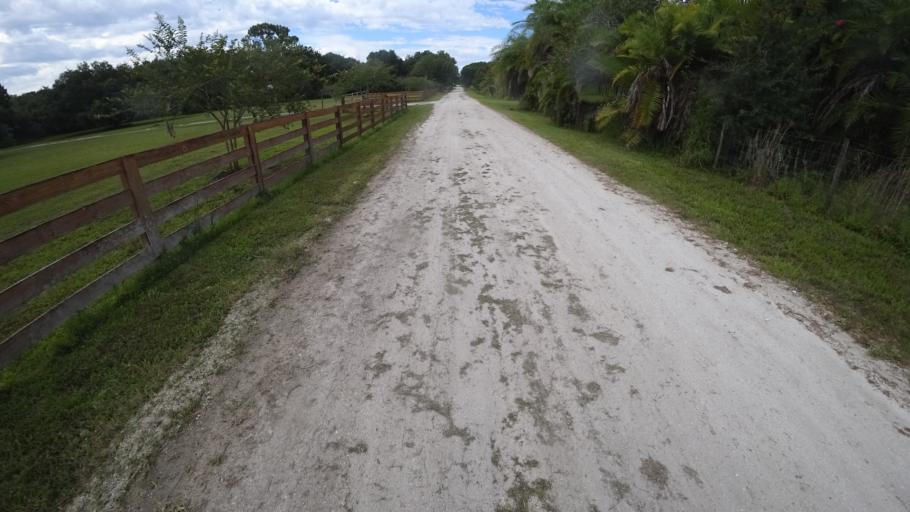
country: US
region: Florida
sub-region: Sarasota County
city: The Meadows
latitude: 27.4550
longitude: -82.2787
